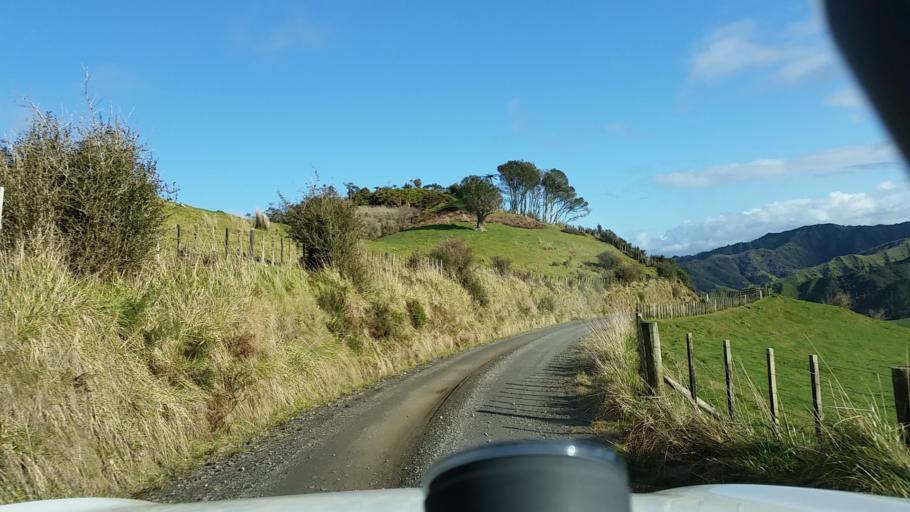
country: NZ
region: Taranaki
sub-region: South Taranaki District
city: Eltham
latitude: -39.4083
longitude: 174.5428
